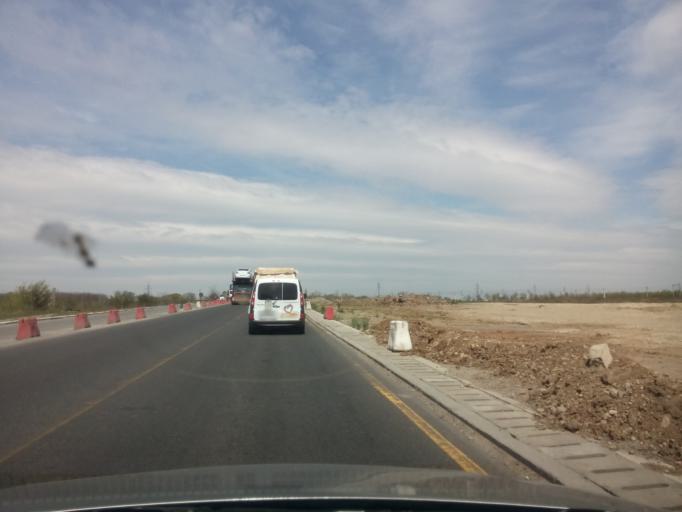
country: RO
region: Ilfov
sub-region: Comuna Pantelimon
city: Pantelimon
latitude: 44.4695
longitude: 26.2322
